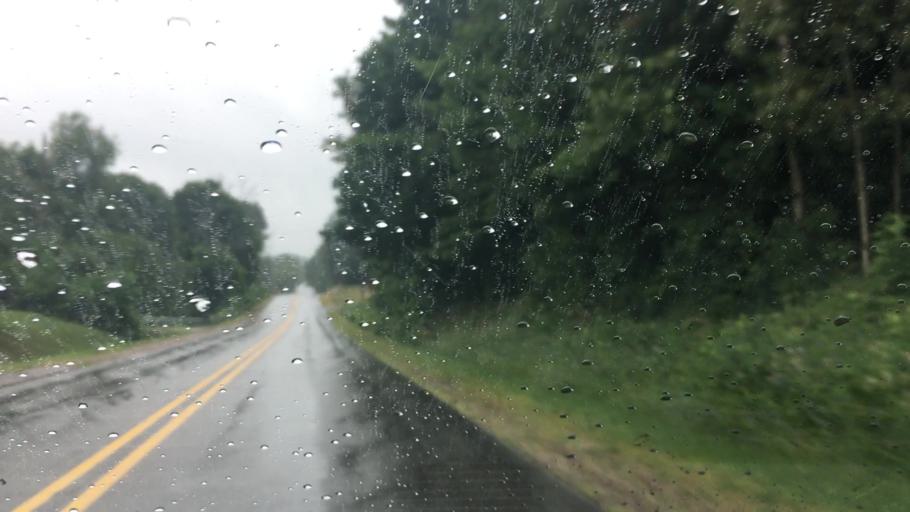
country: US
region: Michigan
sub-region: Ottawa County
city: Hudsonville
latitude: 42.8143
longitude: -85.8421
